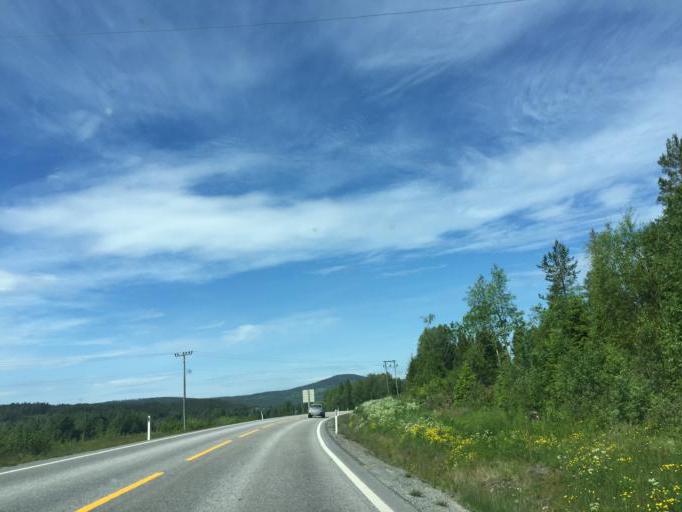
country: NO
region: Hedmark
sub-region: Sor-Odal
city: Skarnes
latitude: 60.2483
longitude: 11.7244
